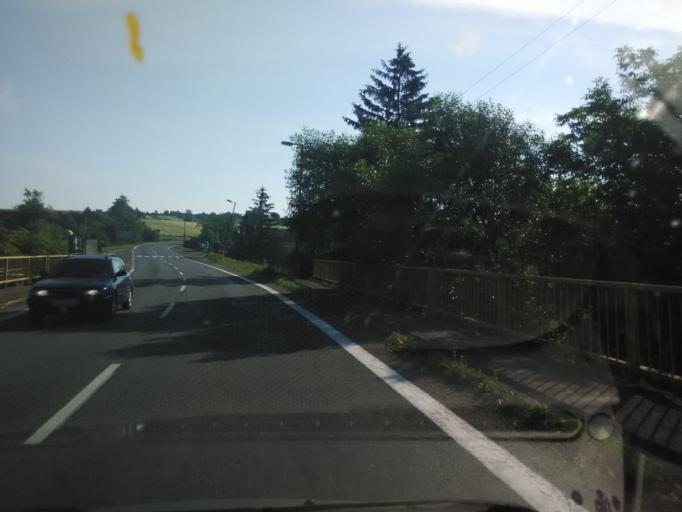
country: SK
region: Nitriansky
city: Levice
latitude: 48.2618
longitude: 18.7071
